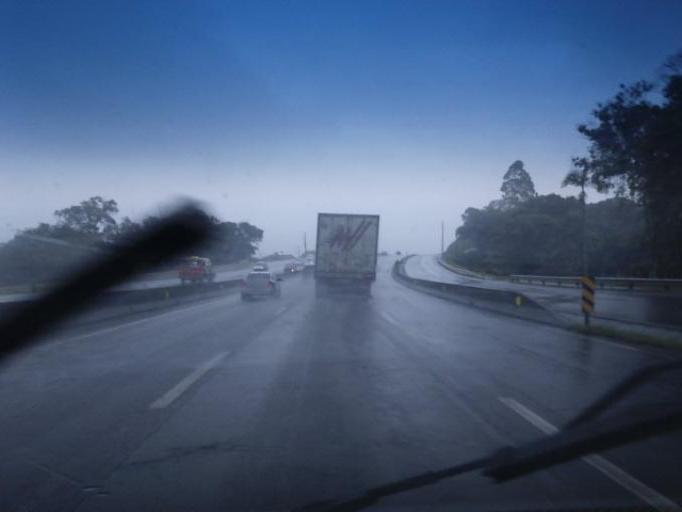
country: BR
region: Santa Catarina
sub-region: Joinville
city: Joinville
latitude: -26.3547
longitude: -48.8588
